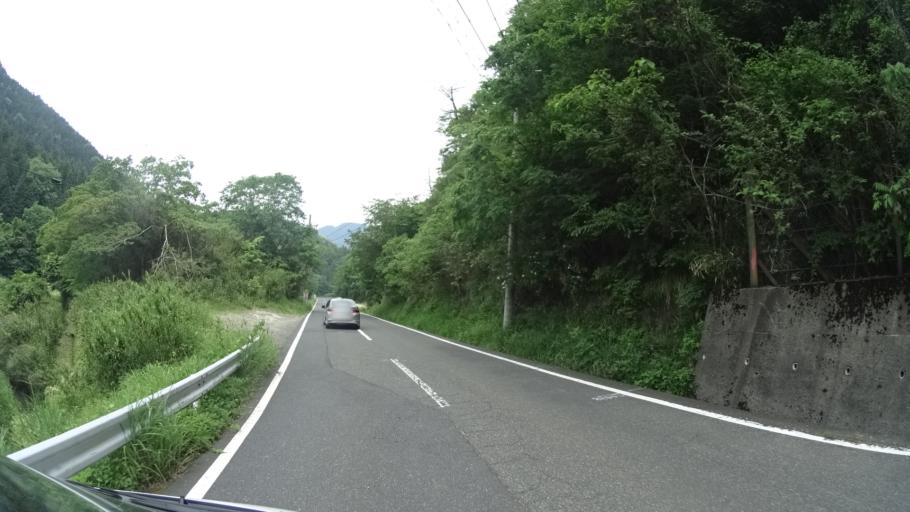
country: JP
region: Kyoto
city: Miyazu
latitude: 35.7111
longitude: 135.2618
